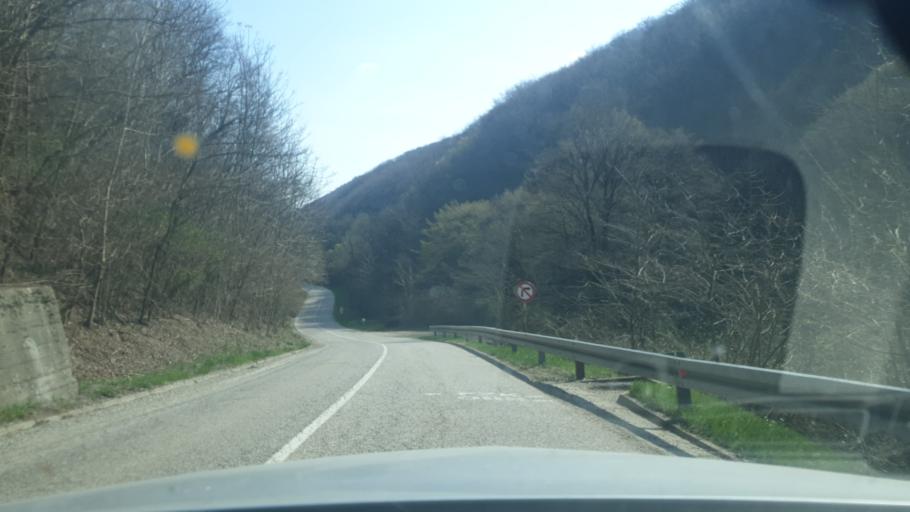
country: RS
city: Vrdnik
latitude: 45.1438
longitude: 19.7714
